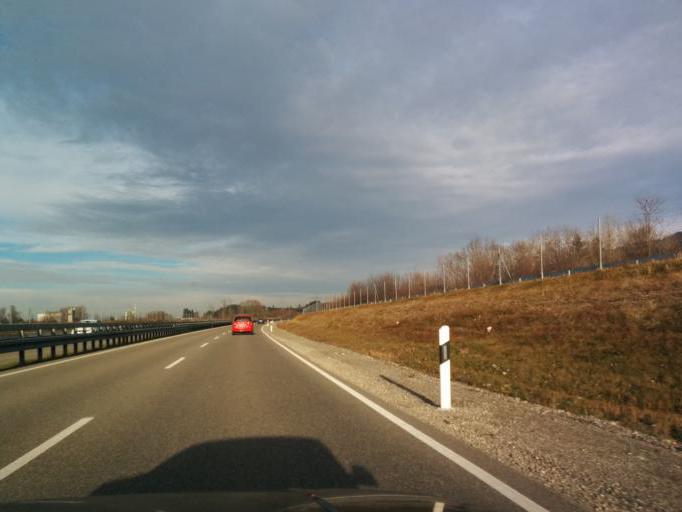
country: DE
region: Bavaria
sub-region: Swabia
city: Rettenberg
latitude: 47.5940
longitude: 10.2627
